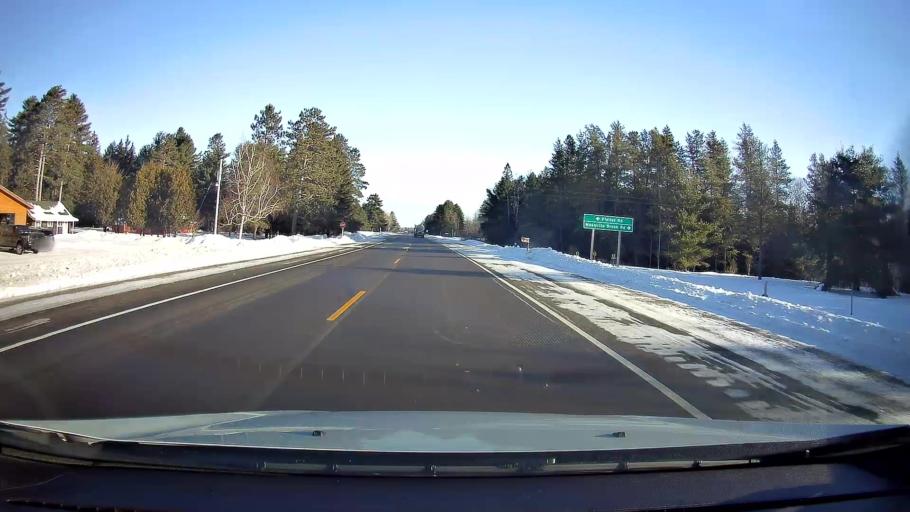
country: US
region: Wisconsin
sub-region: Sawyer County
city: Hayward
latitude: 46.0837
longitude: -91.3979
